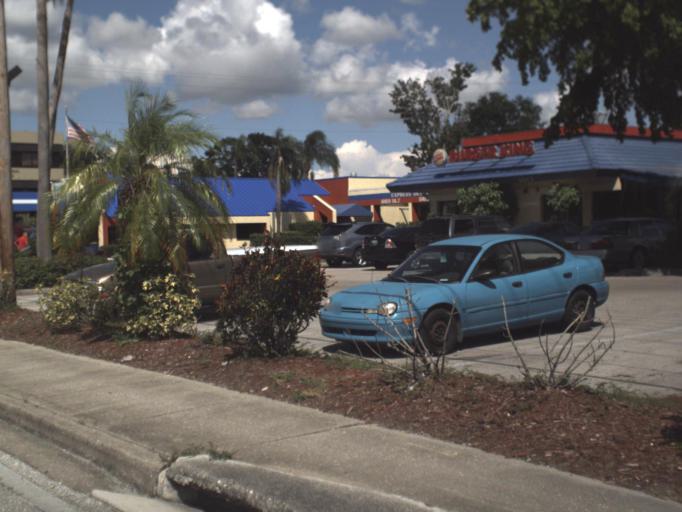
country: US
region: Florida
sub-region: Lee County
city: Lochmoor Waterway Estates
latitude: 26.6330
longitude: -81.9407
